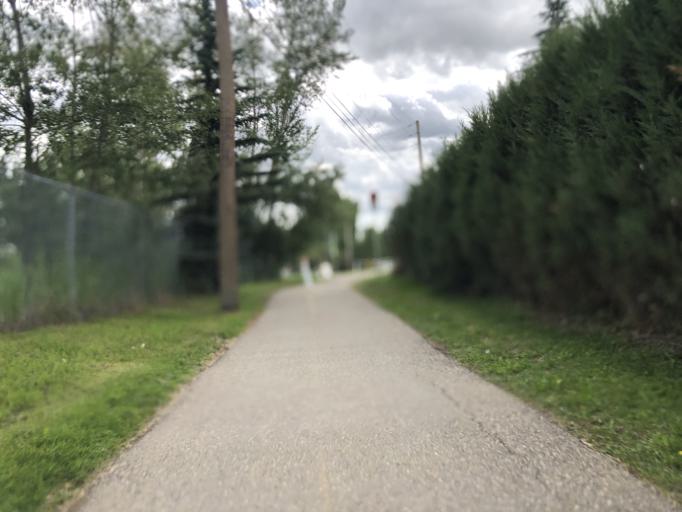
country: CA
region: Alberta
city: Calgary
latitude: 51.0319
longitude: -114.0115
